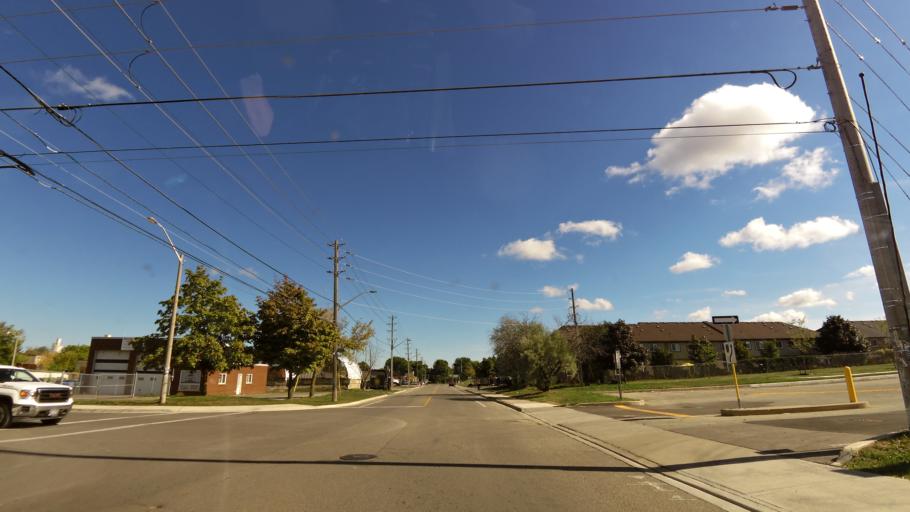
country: CA
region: Ontario
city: Mississauga
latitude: 43.5793
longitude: -79.7183
